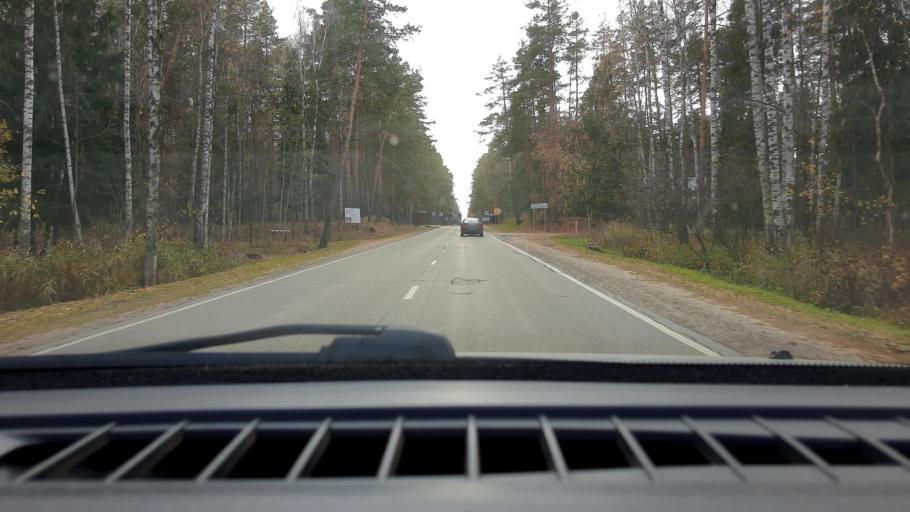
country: RU
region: Nizjnij Novgorod
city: Afonino
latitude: 56.1862
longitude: 44.1127
